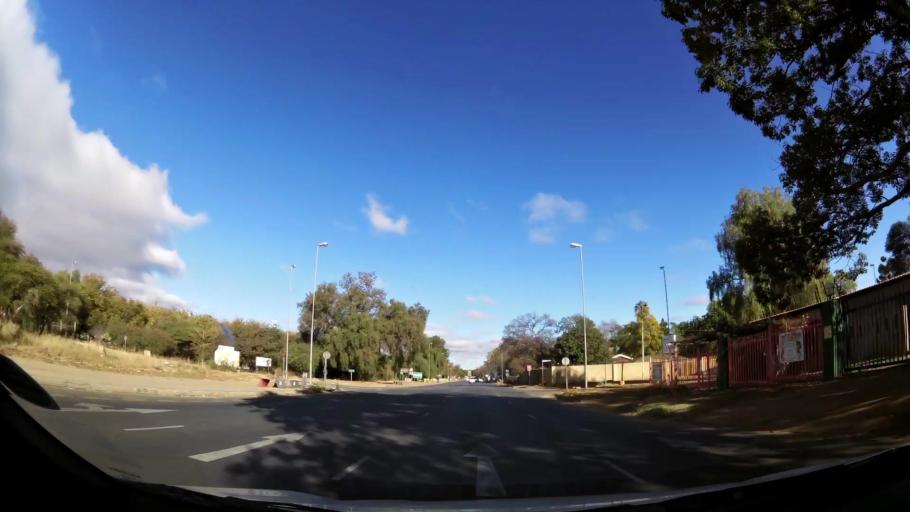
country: ZA
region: Limpopo
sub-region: Capricorn District Municipality
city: Polokwane
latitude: -23.9191
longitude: 29.4608
